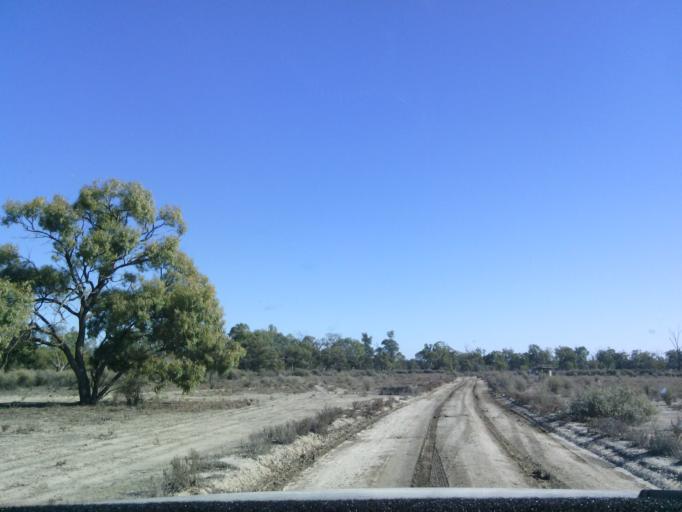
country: AU
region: South Australia
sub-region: Berri and Barmera
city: Berri
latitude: -34.2597
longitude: 140.6924
